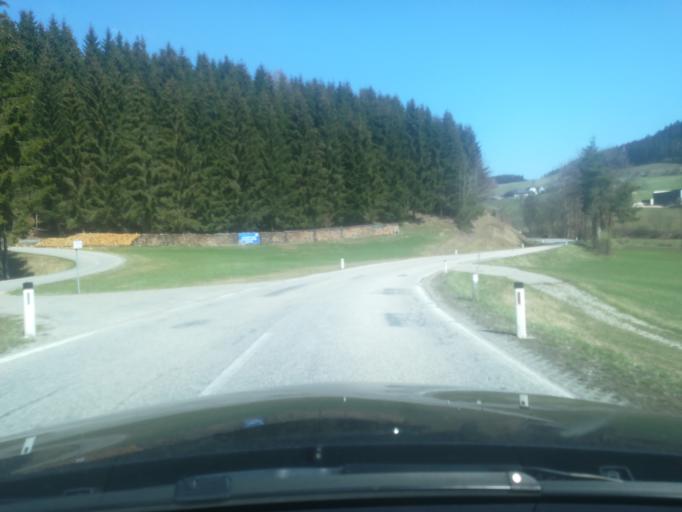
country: AT
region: Upper Austria
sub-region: Politischer Bezirk Perg
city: Sankt Georgen am Walde
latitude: 48.4246
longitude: 14.7720
